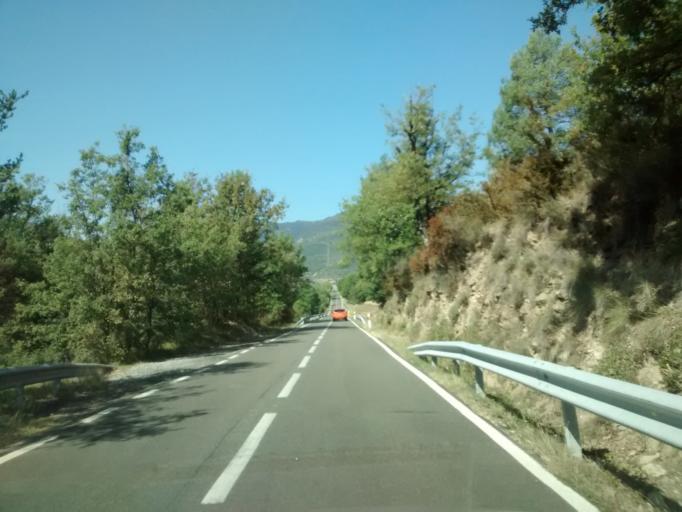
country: ES
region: Aragon
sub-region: Provincia de Huesca
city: Fiscal
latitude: 42.4893
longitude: -0.0951
